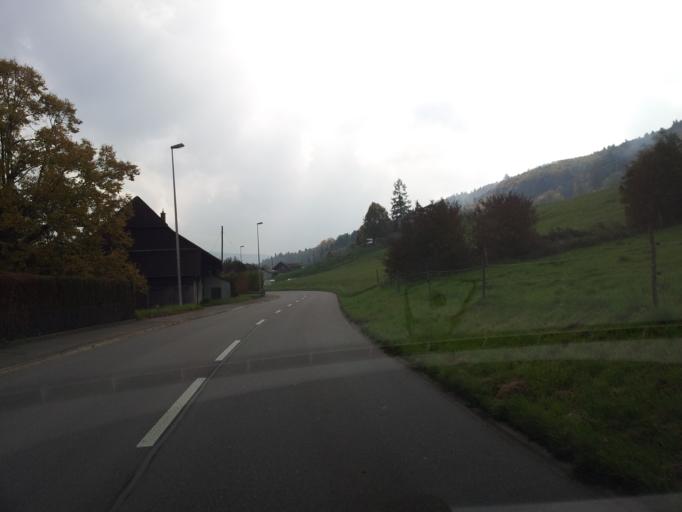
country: CH
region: Bern
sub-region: Bern-Mittelland District
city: Belp
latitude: 46.9005
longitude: 7.4863
